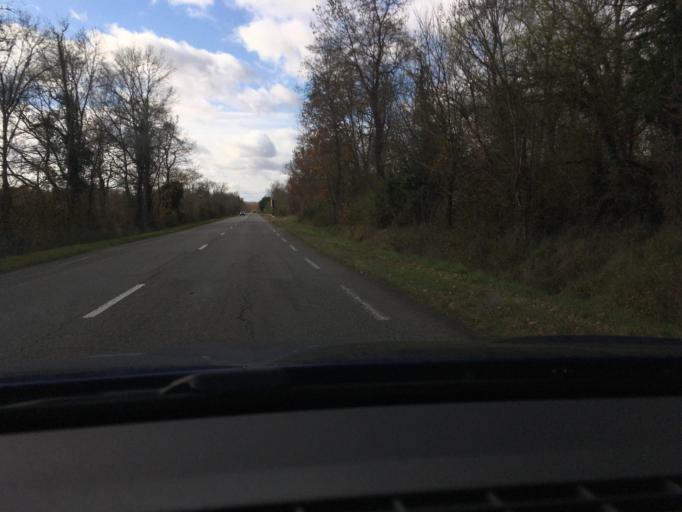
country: FR
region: Midi-Pyrenees
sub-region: Departement du Tarn-et-Garonne
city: Monteils
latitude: 44.1694
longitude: 1.5828
